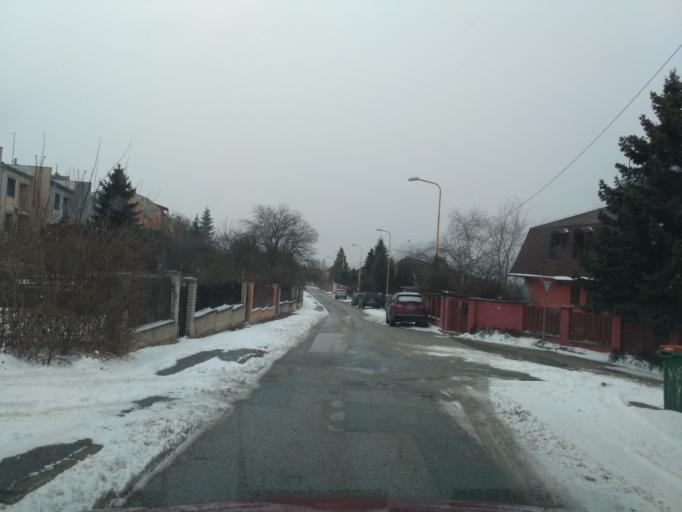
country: SK
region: Kosicky
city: Kosice
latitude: 48.7168
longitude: 21.2215
